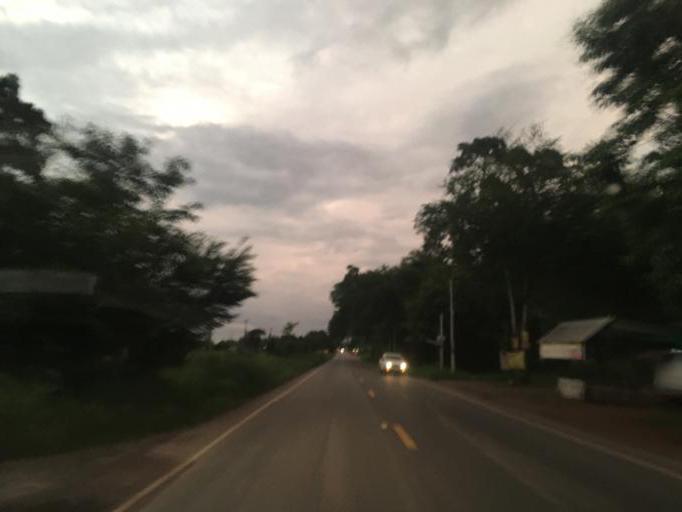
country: TH
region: Changwat Udon Thani
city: Udon Thani
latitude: 17.3585
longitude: 102.7203
